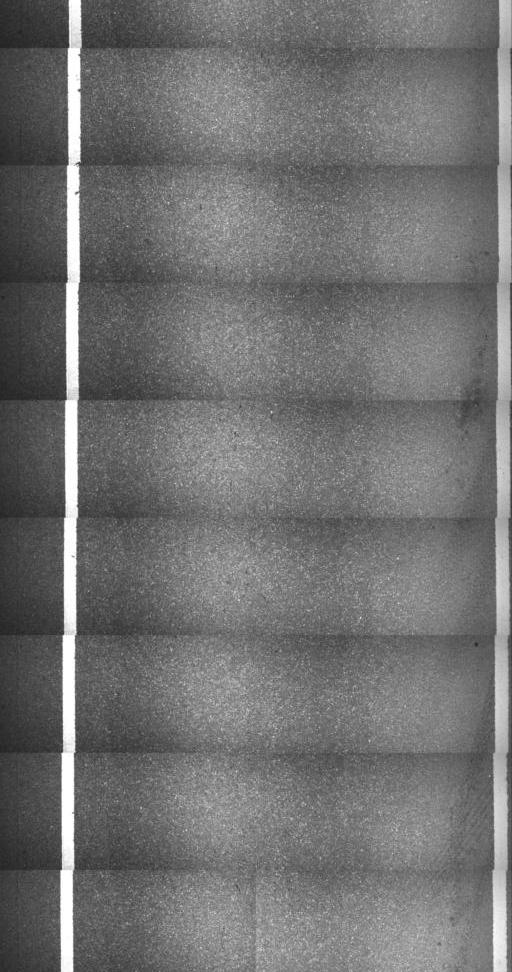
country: US
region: Vermont
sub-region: Washington County
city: Waterbury
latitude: 44.3232
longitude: -72.7521
